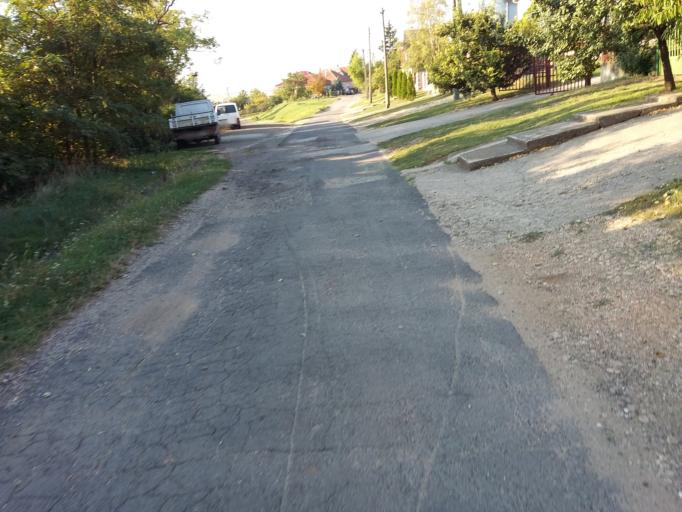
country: HU
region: Borsod-Abauj-Zemplen
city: Bekecs
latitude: 48.1577
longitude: 21.1770
